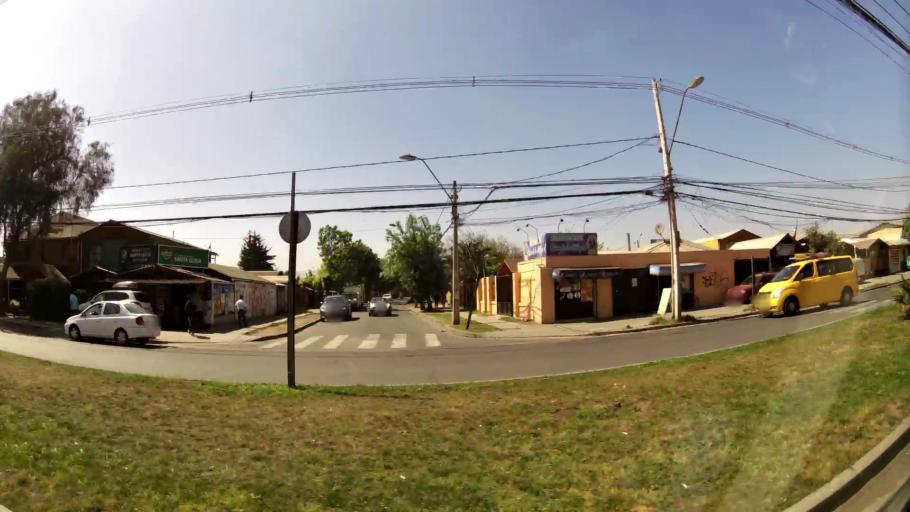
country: CL
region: Santiago Metropolitan
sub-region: Provincia de Santiago
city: Lo Prado
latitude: -33.3593
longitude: -70.7369
